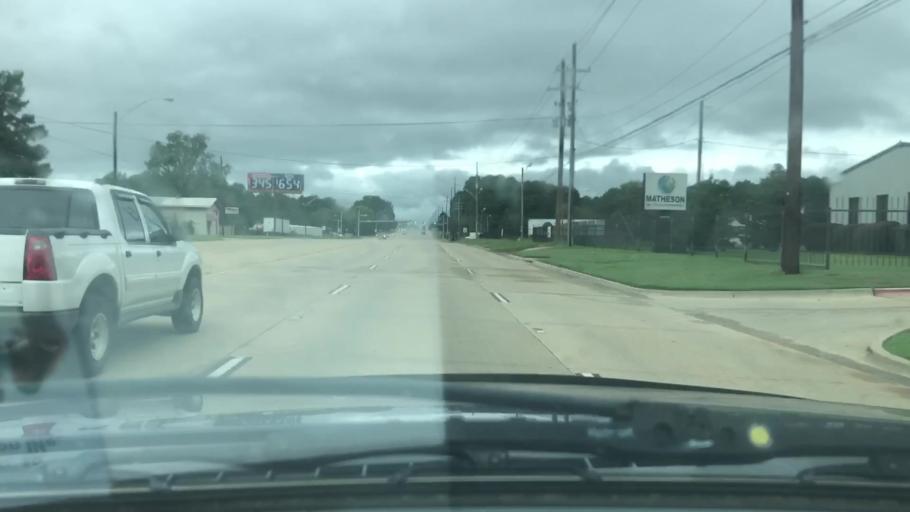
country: US
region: Texas
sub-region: Bowie County
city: Wake Village
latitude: 33.4213
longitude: -94.0772
